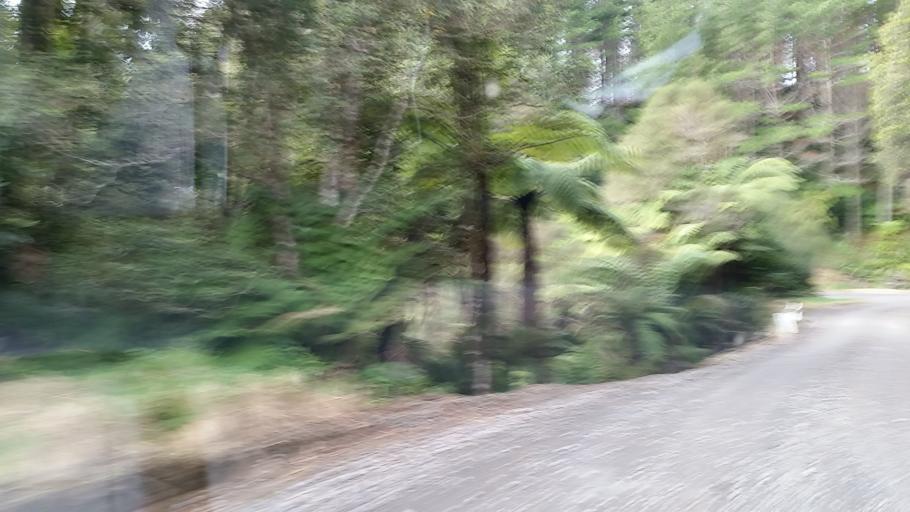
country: NZ
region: Taranaki
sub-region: New Plymouth District
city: Waitara
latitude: -39.1575
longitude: 174.5538
